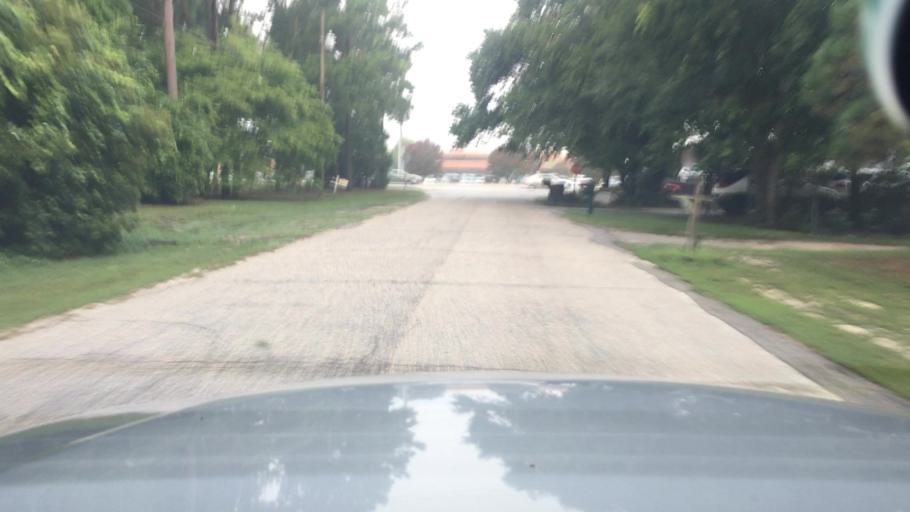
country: US
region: North Carolina
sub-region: Cumberland County
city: Hope Mills
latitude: 35.0134
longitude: -78.9179
